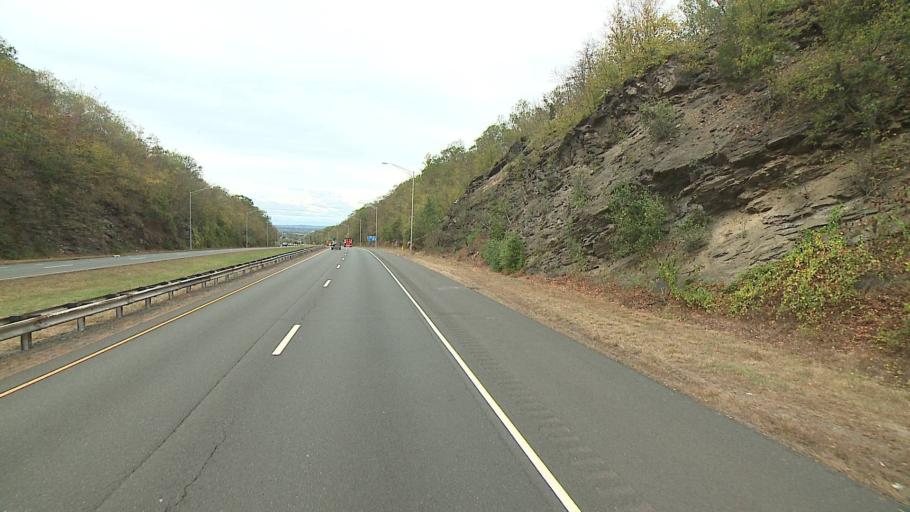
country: US
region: Connecticut
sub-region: Middlesex County
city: Higganum
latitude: 41.5231
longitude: -72.6071
